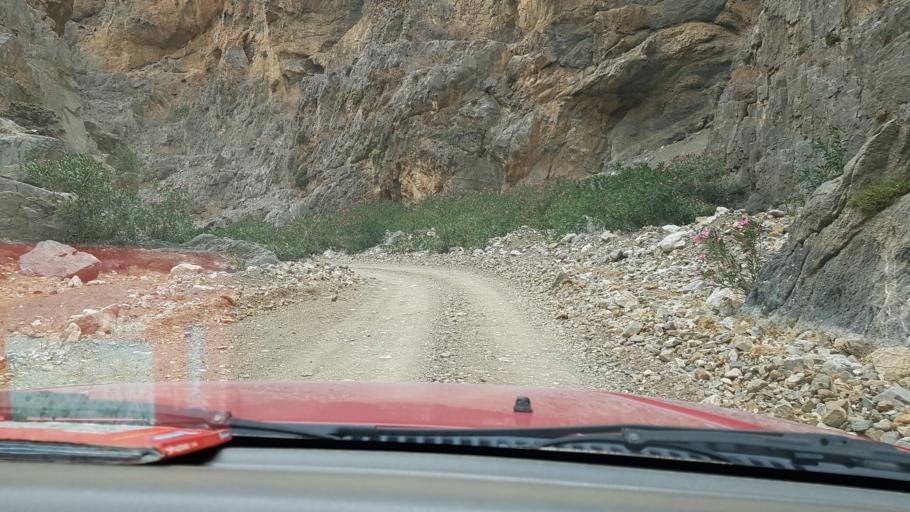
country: GR
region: Crete
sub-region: Nomos Irakleiou
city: Agioi Deka
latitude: 34.9424
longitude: 24.9843
